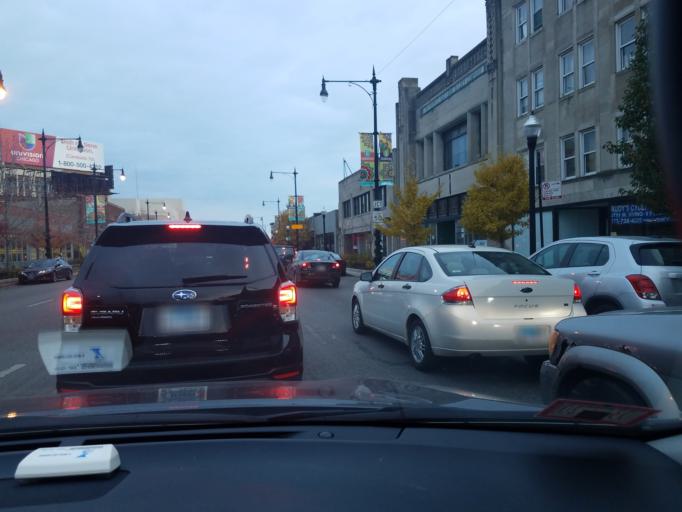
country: US
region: Illinois
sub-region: Cook County
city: Lincolnwood
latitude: 41.9534
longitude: -87.7493
